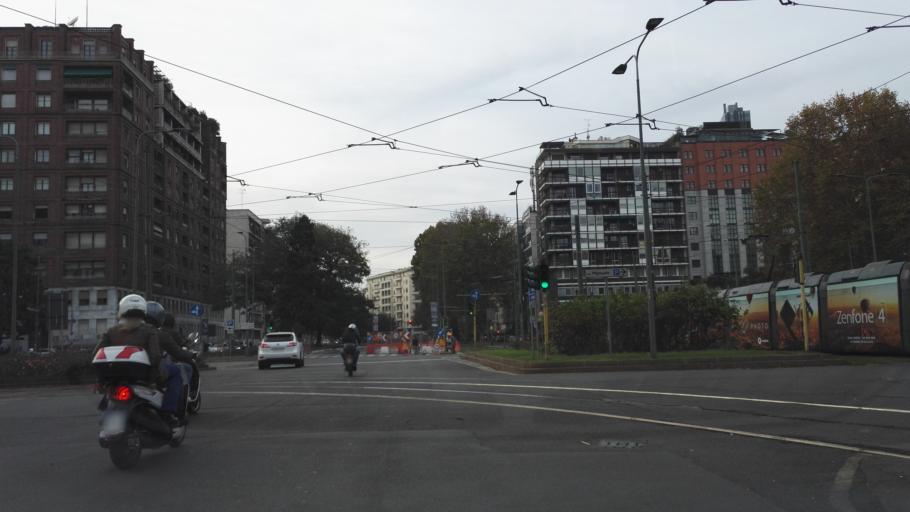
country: IT
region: Lombardy
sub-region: Citta metropolitana di Milano
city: Milano
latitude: 45.4780
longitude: 9.1972
